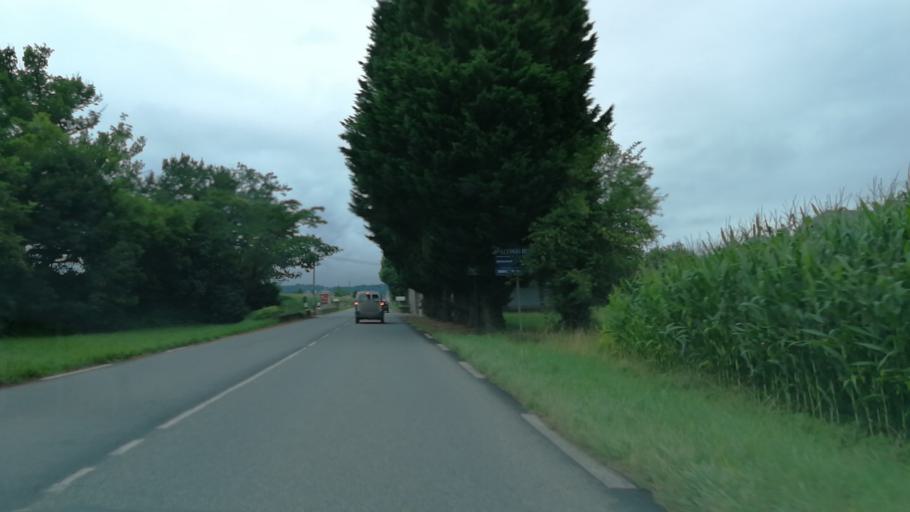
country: FR
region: Aquitaine
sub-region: Departement des Pyrenees-Atlantiques
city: Oloron-Sainte-Marie
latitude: 43.1420
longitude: -0.6032
